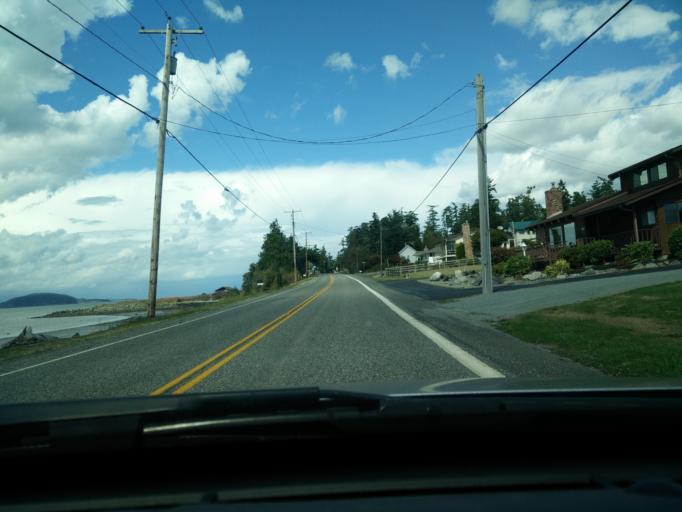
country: US
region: Washington
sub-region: Skagit County
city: Anacortes
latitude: 48.4854
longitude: -122.4788
